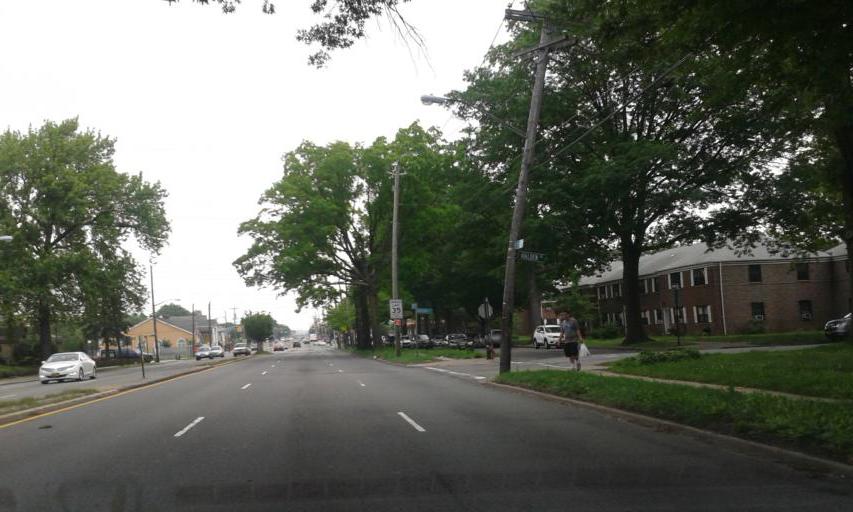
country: US
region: New York
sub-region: Richmond County
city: Staten Island
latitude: 40.5625
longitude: -74.1178
